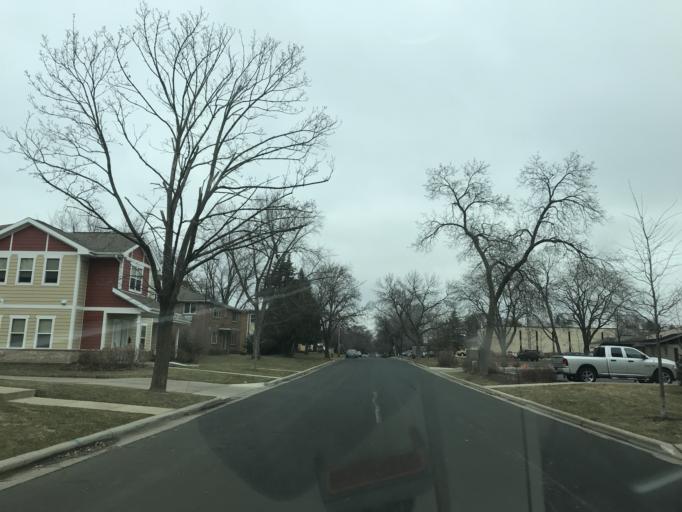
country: US
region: Wisconsin
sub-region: Dane County
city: Monona
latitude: 43.0652
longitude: -89.3272
